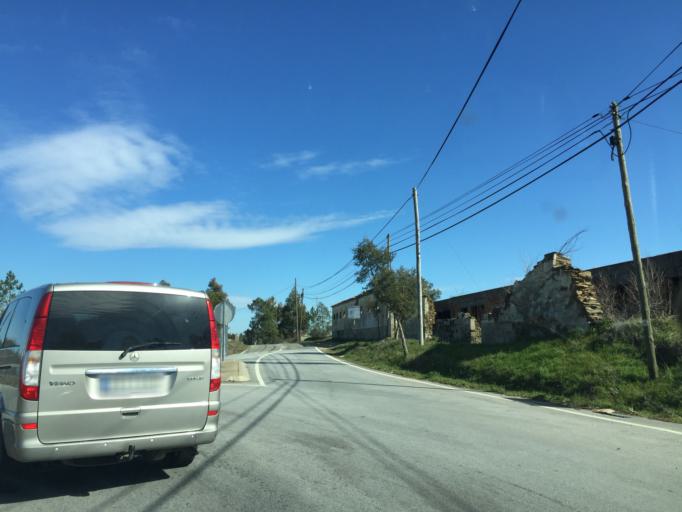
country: PT
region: Castelo Branco
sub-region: Castelo Branco
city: Castelo Branco
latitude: 39.7844
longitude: -7.5696
